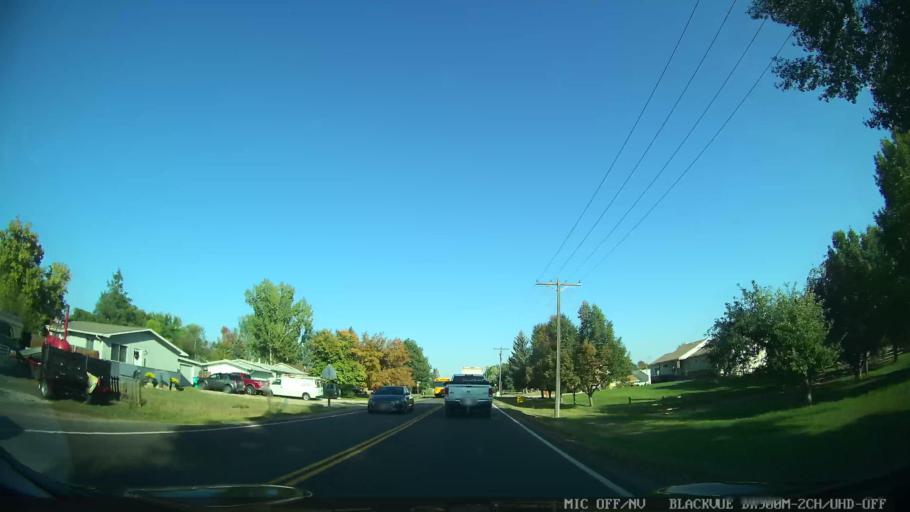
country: US
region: Colorado
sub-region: Larimer County
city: Loveland
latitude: 40.4510
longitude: -105.0659
